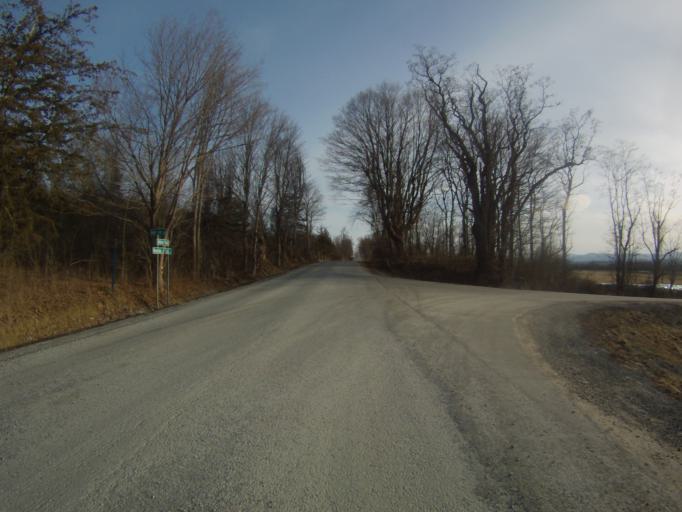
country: US
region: Vermont
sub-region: Addison County
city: Middlebury (village)
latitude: 44.0315
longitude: -73.2943
